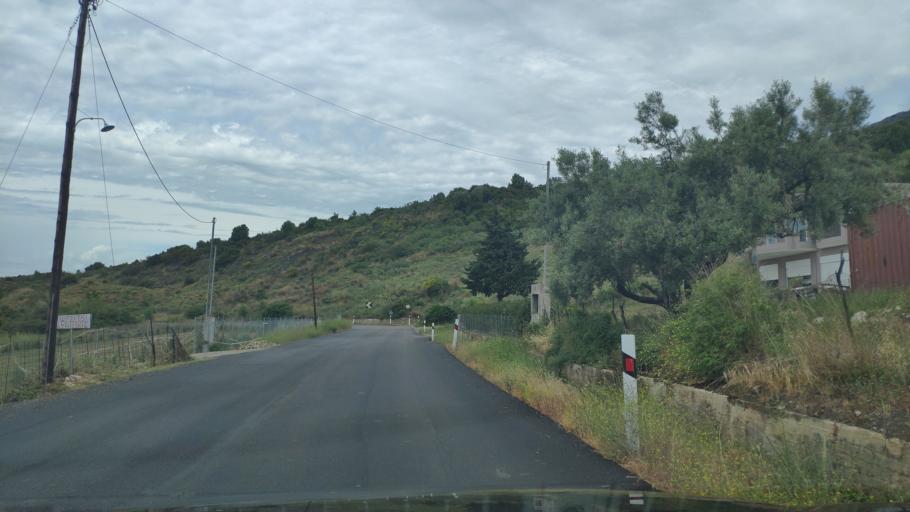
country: GR
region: West Greece
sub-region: Nomos Aitolias kai Akarnanias
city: Palairos
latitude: 38.7569
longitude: 20.8862
